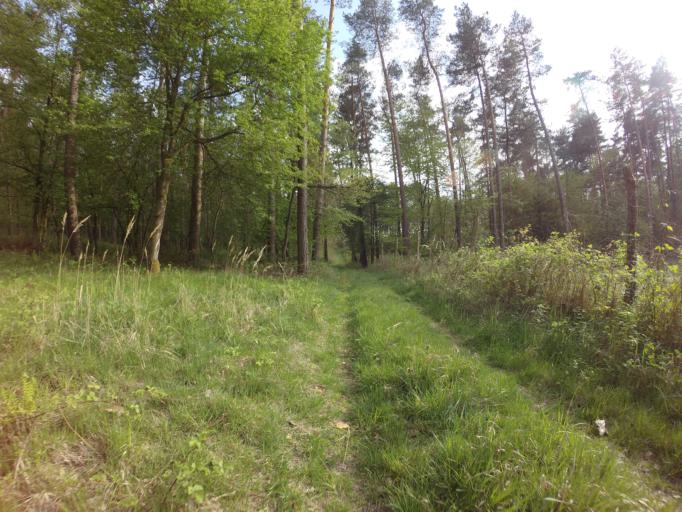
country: PL
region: West Pomeranian Voivodeship
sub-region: Powiat choszczenski
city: Choszczno
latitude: 53.1531
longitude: 15.3285
